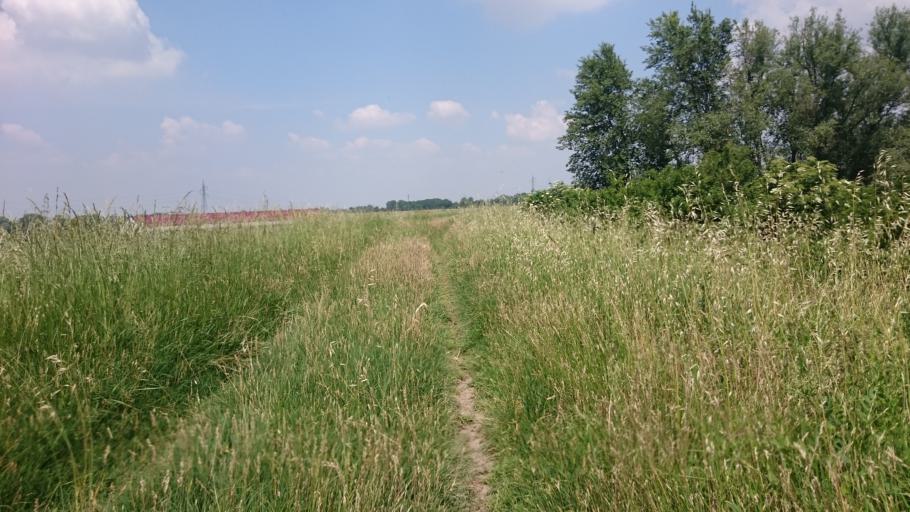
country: IT
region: Lombardy
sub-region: Provincia di Mantova
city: San Biagio
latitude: 45.1172
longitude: 10.8523
